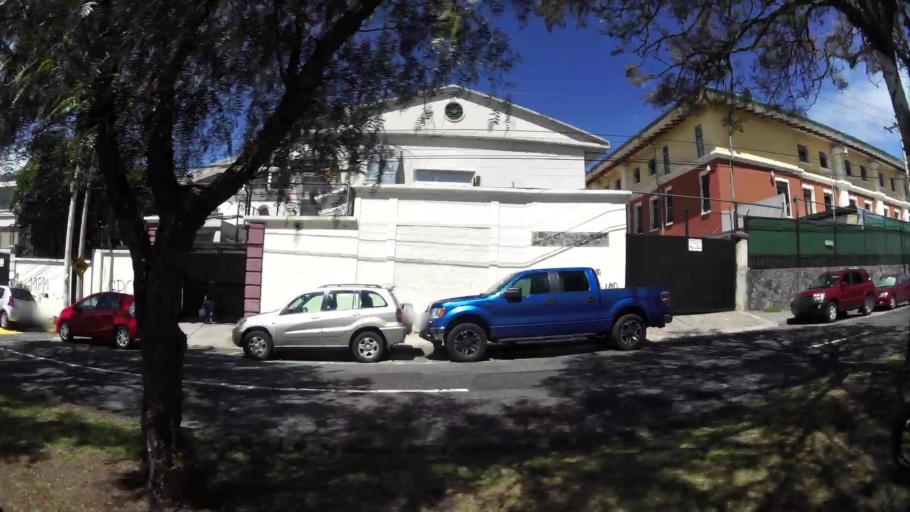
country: EC
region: Pichincha
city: Quito
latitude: -0.1958
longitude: -78.4348
